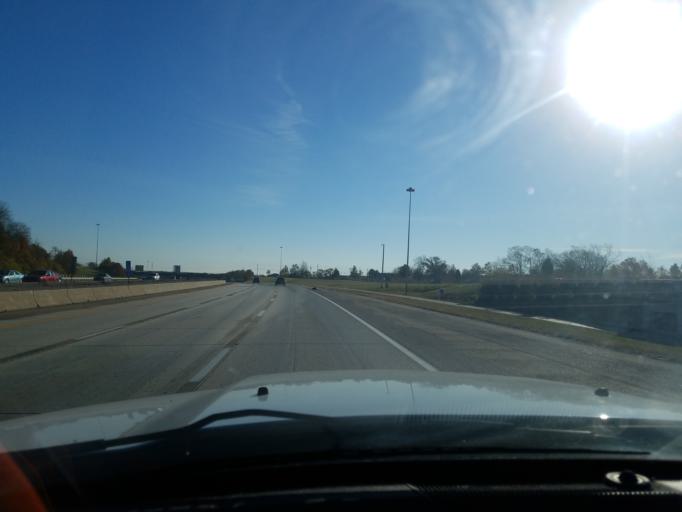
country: US
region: Kentucky
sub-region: Kenton County
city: Lakeside Park
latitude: 39.0271
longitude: -84.5746
